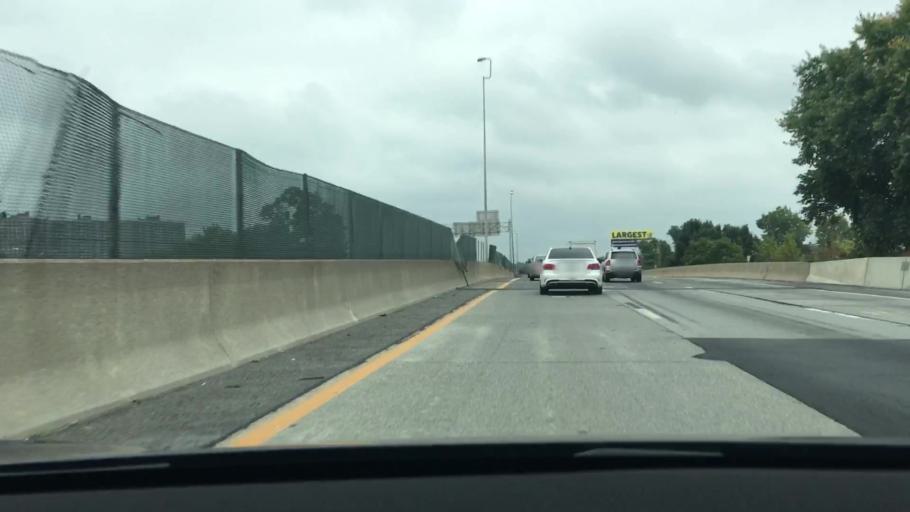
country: US
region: New York
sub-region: Bronx
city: Eastchester
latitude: 40.8690
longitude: -73.8330
